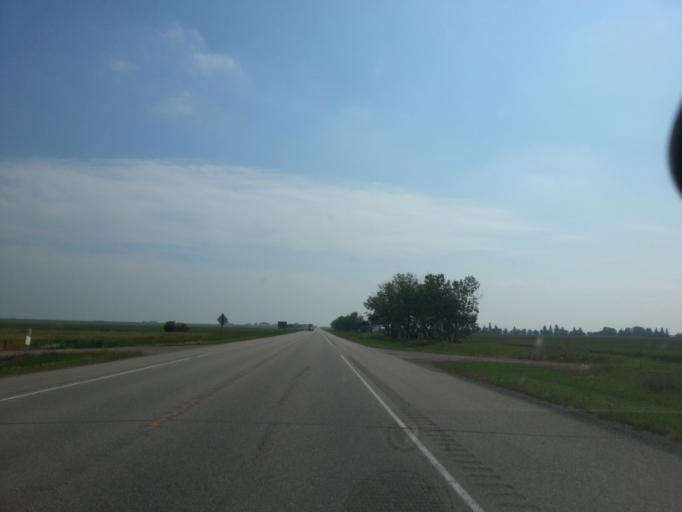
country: CA
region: Alberta
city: Irricana
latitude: 51.3869
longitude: -113.5102
